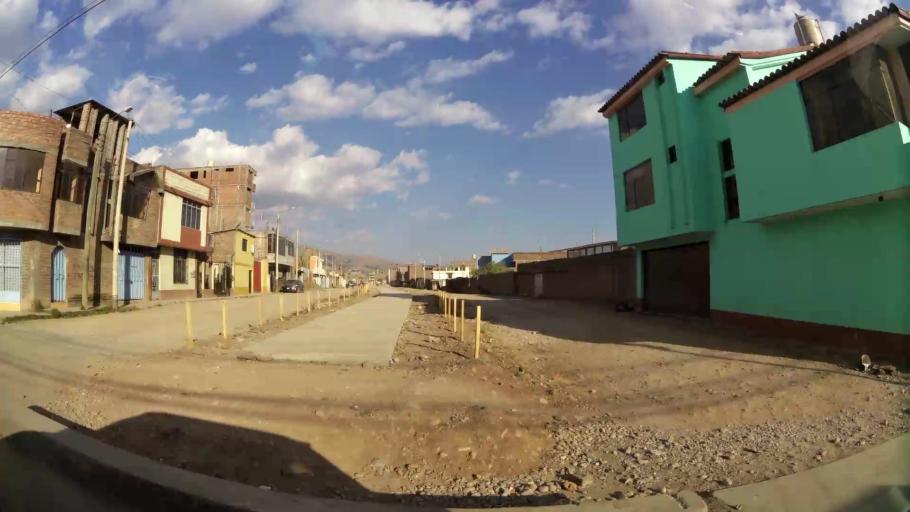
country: PE
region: Junin
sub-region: Provincia de Huancayo
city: El Tambo
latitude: -12.0502
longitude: -75.2193
